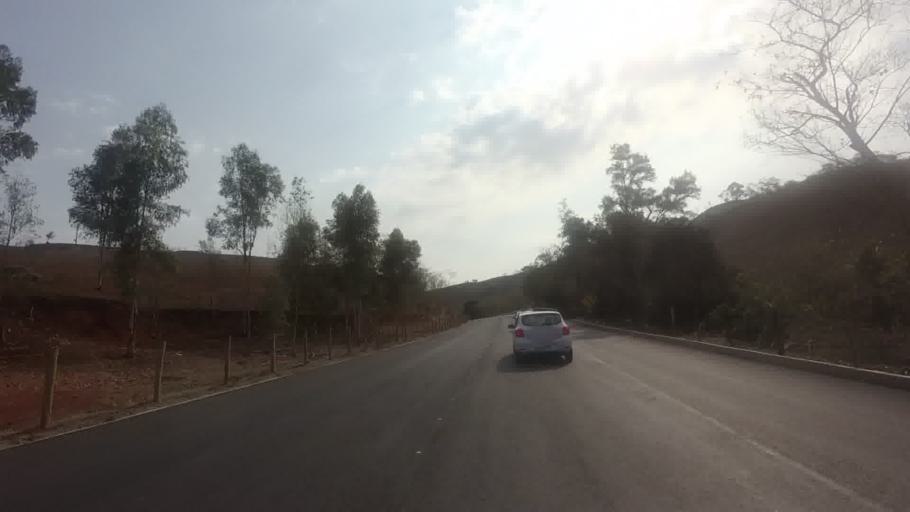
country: BR
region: Rio de Janeiro
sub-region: Bom Jesus Do Itabapoana
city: Bom Jesus do Itabapoana
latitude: -21.1981
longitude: -41.7125
